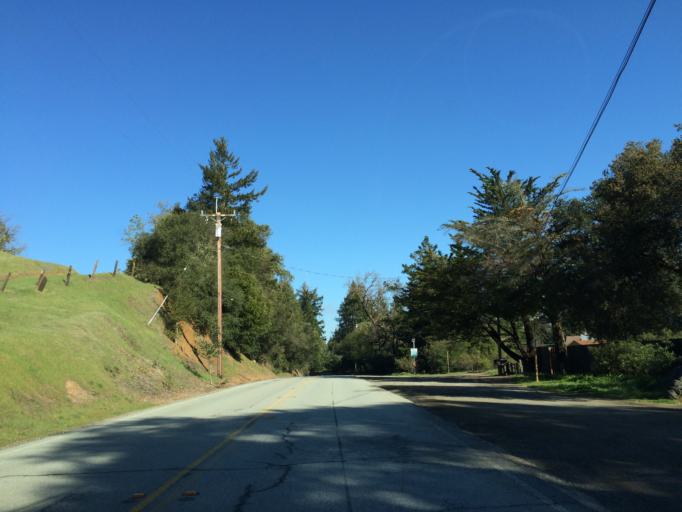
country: US
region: California
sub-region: Santa Clara County
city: Loyola
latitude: 37.2850
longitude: -122.1522
